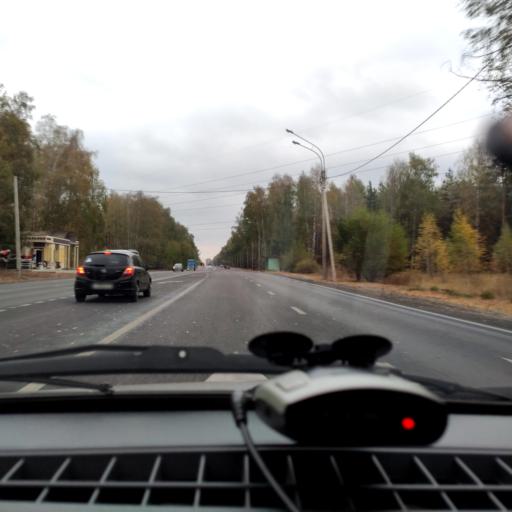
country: RU
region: Voronezj
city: Pridonskoy
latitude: 51.6919
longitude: 39.0975
